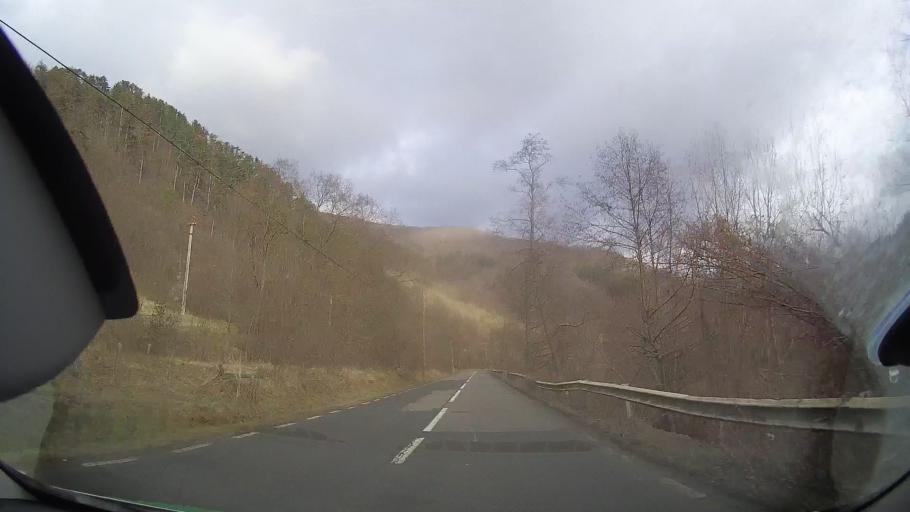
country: RO
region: Cluj
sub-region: Comuna Iara
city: Iara
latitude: 46.5012
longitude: 23.5412
